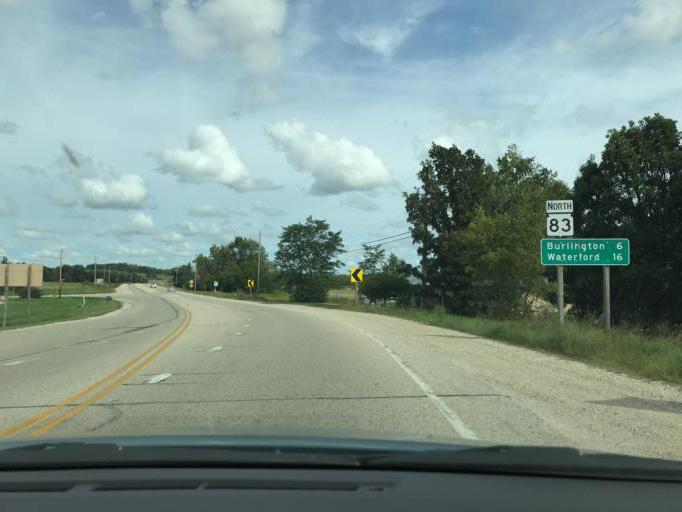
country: US
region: Wisconsin
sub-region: Kenosha County
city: Twin Lakes
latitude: 42.5827
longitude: -88.2179
